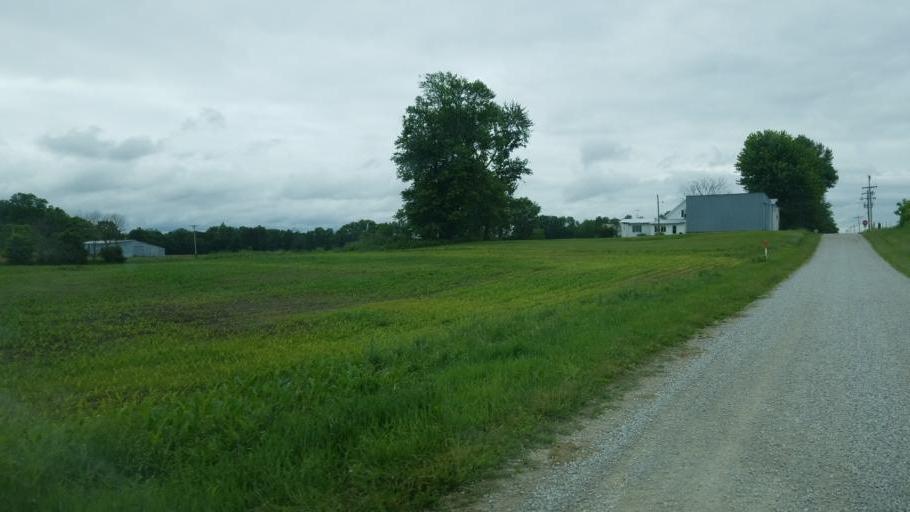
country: US
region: Ohio
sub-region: Morrow County
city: Mount Gilead
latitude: 40.5166
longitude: -82.7782
